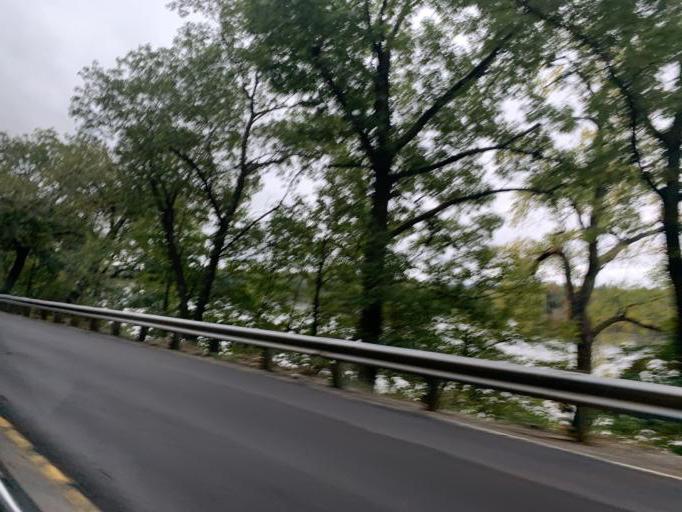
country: US
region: Wisconsin
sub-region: Grant County
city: Muscoda
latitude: 43.2086
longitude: -90.3654
